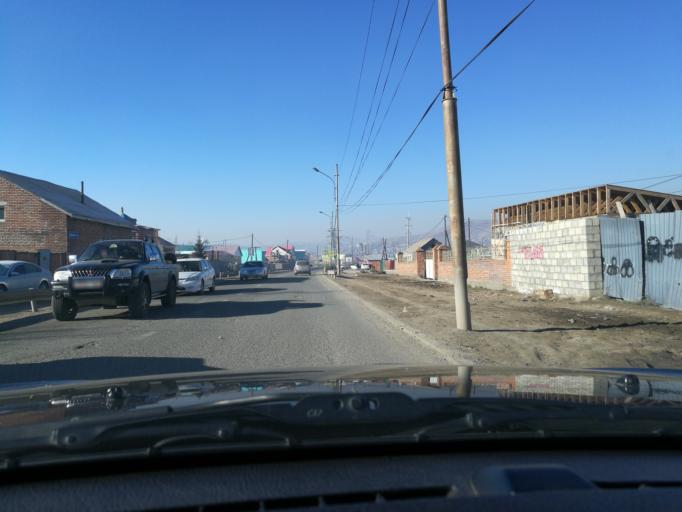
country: MN
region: Ulaanbaatar
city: Ulaanbaatar
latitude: 47.9799
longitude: 106.9367
